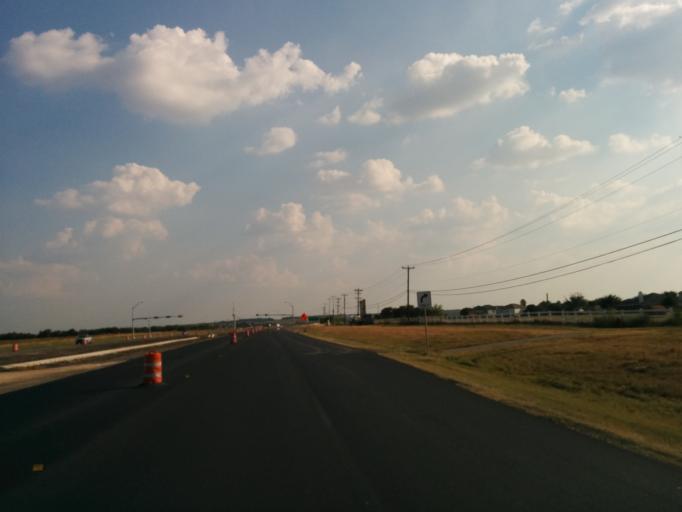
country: US
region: Texas
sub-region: Bexar County
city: Converse
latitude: 29.5007
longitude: -98.2890
